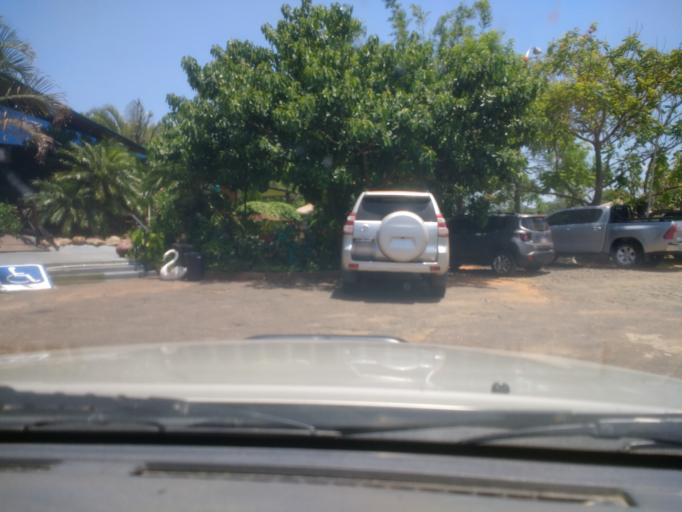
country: PY
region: San Pedro
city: Guayaybi
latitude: -24.6682
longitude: -56.4619
